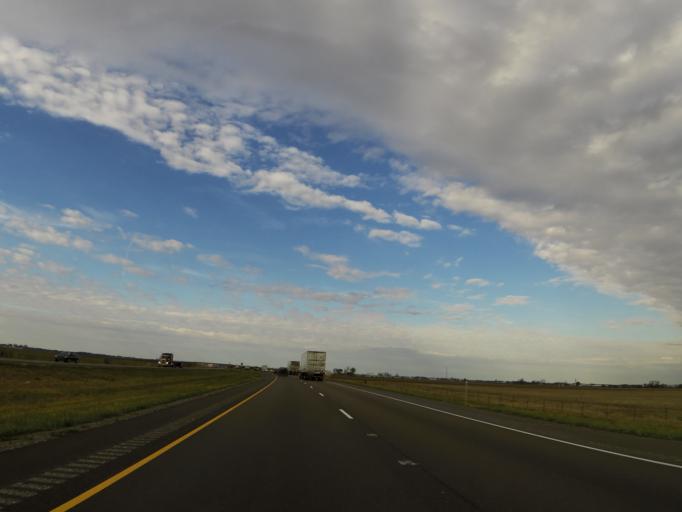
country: US
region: Illinois
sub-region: Washington County
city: Okawville
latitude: 38.4271
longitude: -89.4659
